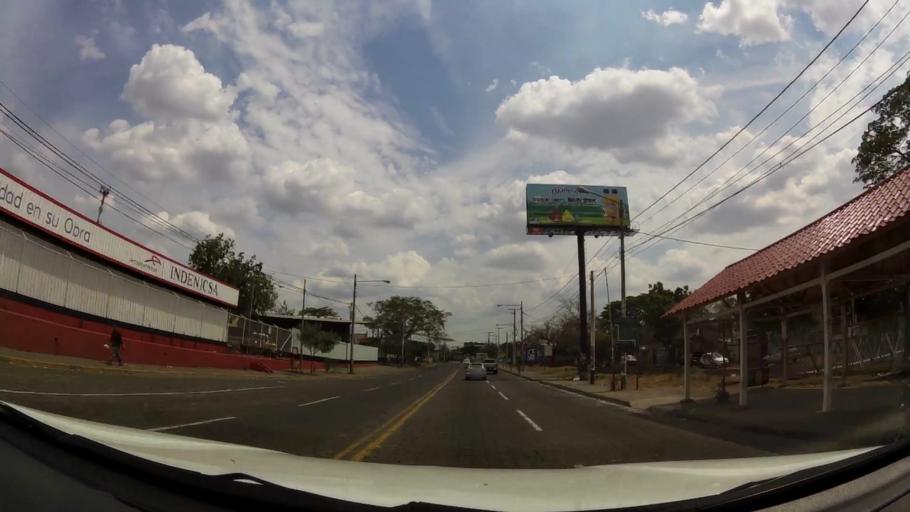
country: NI
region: Managua
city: Managua
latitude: 12.1424
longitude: -86.2421
